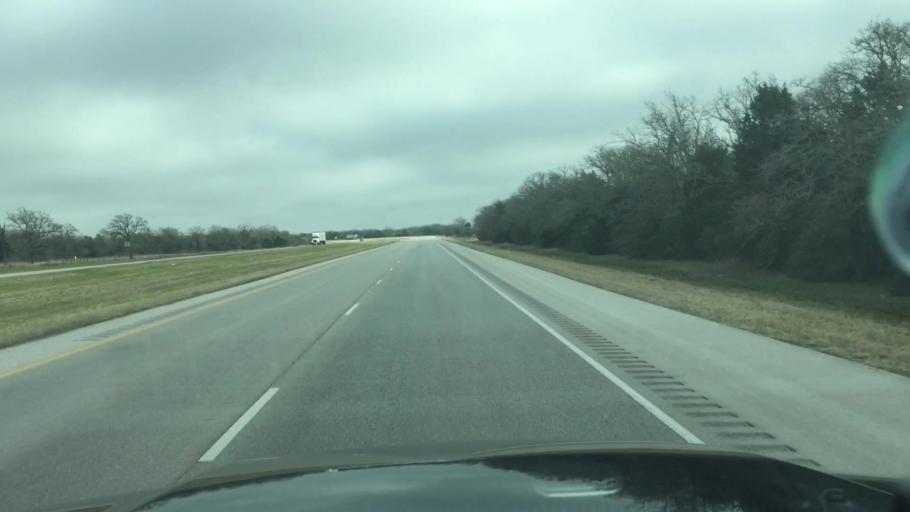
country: US
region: Texas
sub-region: Lee County
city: Giddings
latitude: 30.1429
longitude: -96.7718
